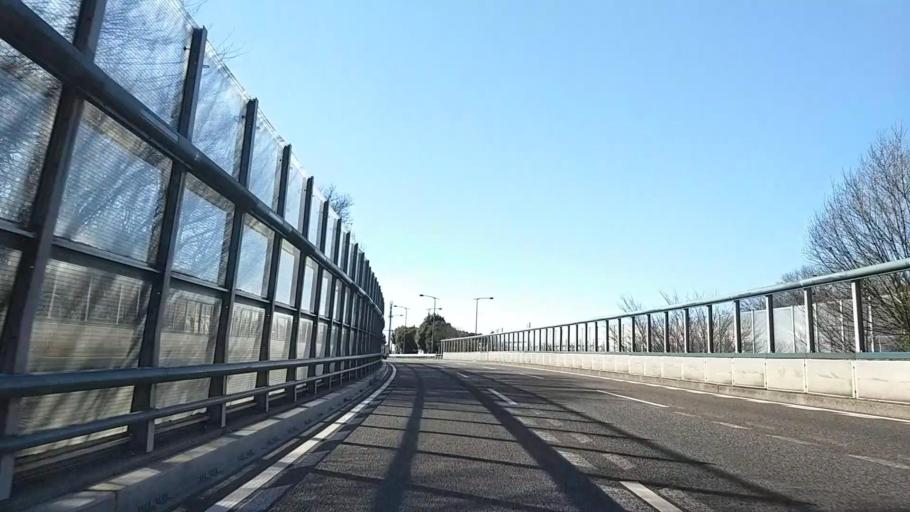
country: JP
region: Kanagawa
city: Yokohama
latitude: 35.4677
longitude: 139.5665
